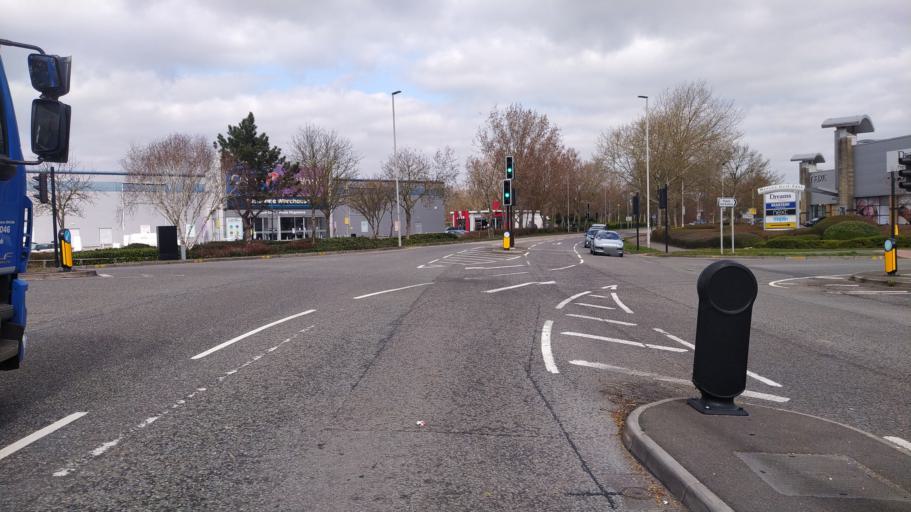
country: GB
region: England
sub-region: Poole
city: Poole
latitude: 50.7348
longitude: -1.9908
